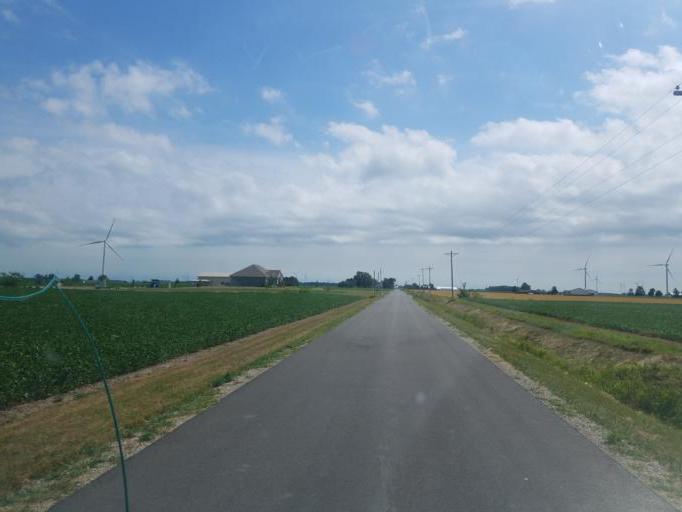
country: US
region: Ohio
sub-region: Paulding County
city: Payne
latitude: 41.1054
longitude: -84.7652
